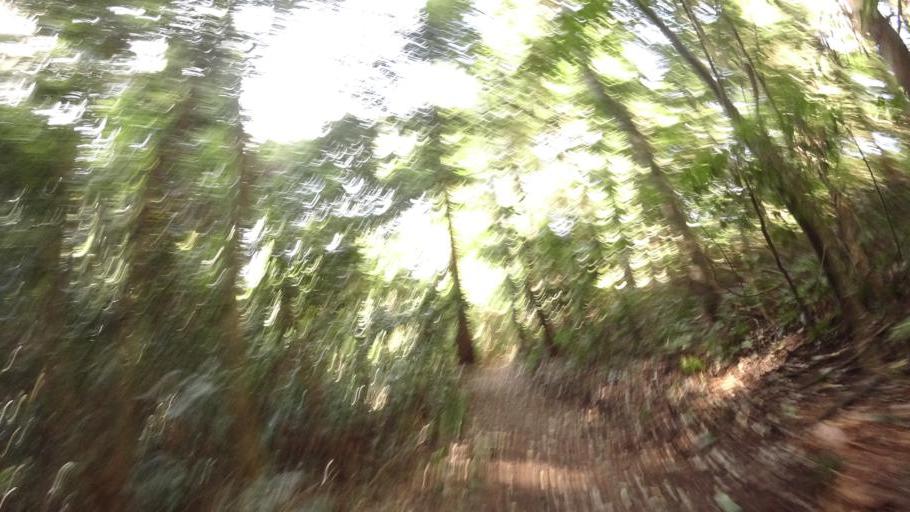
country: AU
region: Queensland
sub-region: Moreton Bay
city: Highvale
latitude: -27.4012
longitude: 152.7954
